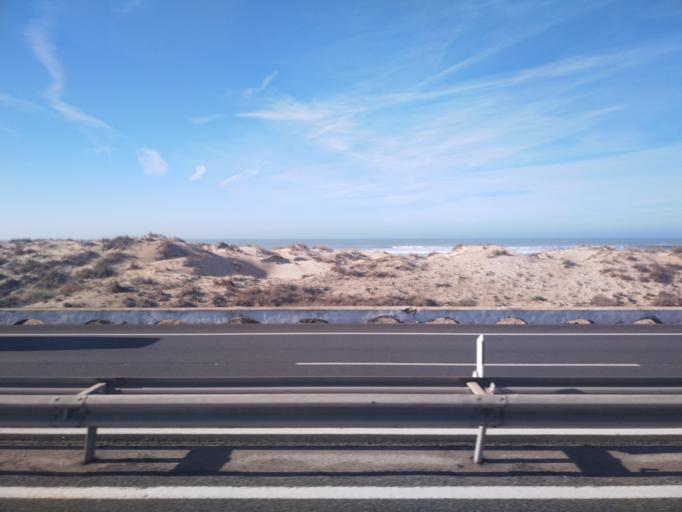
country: ES
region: Andalusia
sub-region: Provincia de Cadiz
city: Cadiz
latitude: 36.4776
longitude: -6.2605
